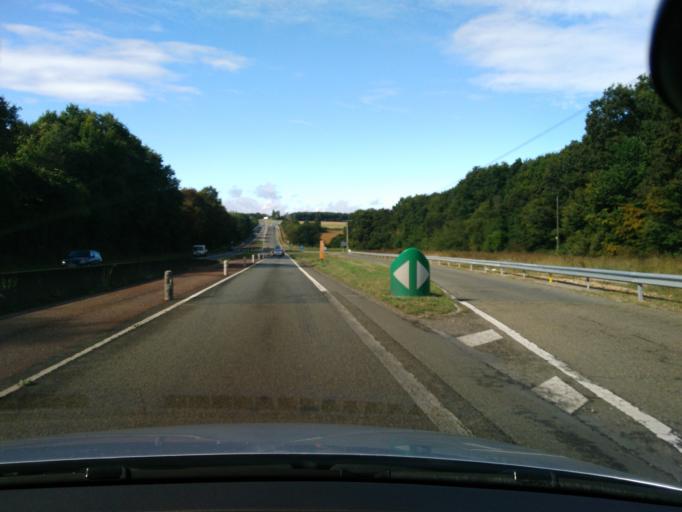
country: FR
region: Centre
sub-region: Departement d'Eure-et-Loir
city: Vert-en-Drouais
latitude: 48.7430
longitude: 1.3255
